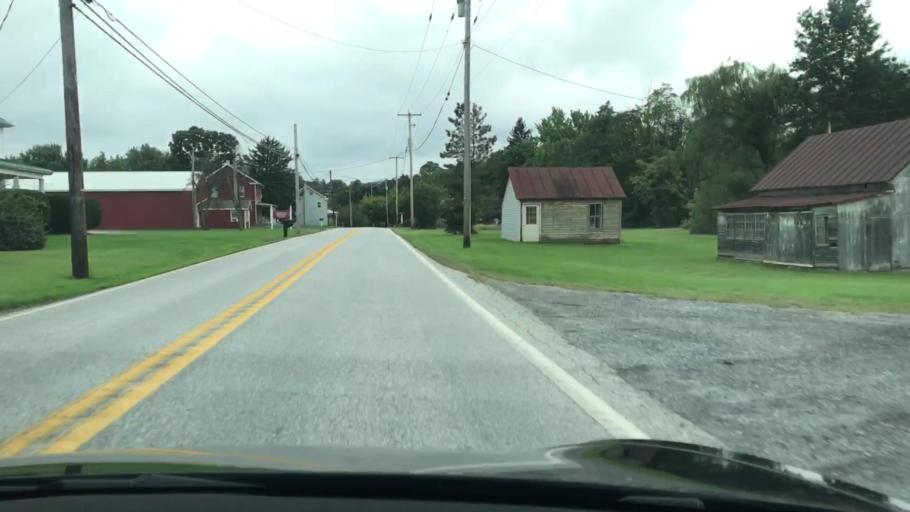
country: US
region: Pennsylvania
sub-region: York County
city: Dillsburg
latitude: 40.1459
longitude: -76.9658
